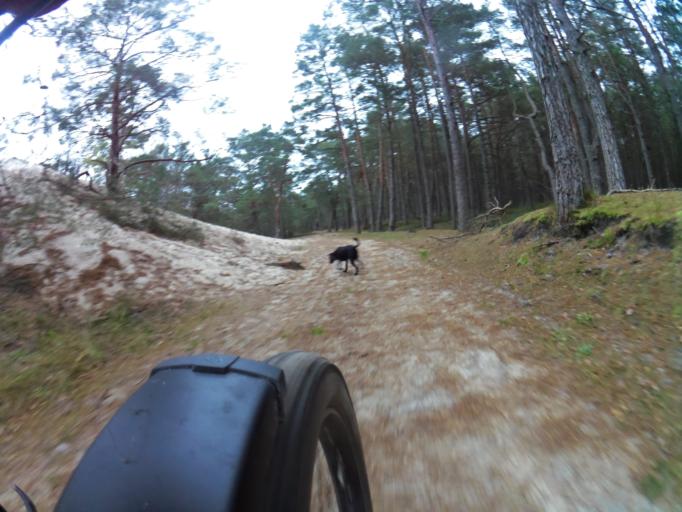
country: PL
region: Pomeranian Voivodeship
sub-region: Powiat wejherowski
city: Choczewo
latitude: 54.7822
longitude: 17.7303
